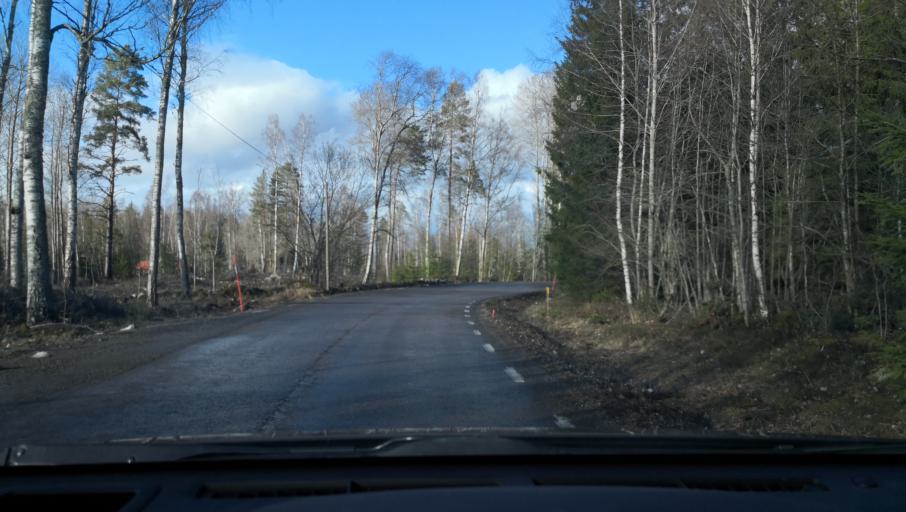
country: SE
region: Vaestmanland
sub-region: Arboga Kommun
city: Arboga
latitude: 59.3545
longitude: 15.8381
